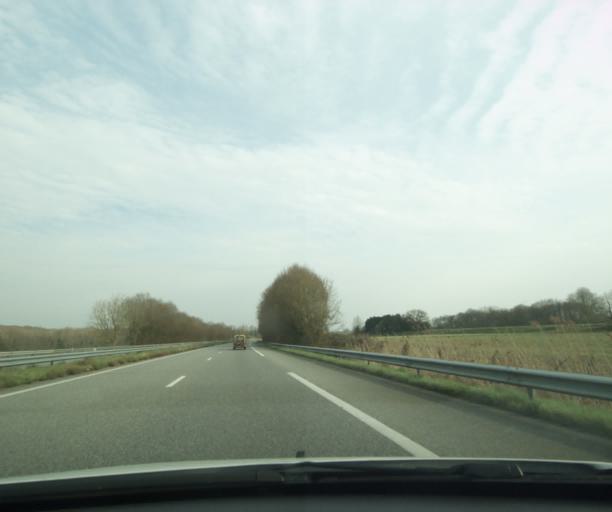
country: FR
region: Aquitaine
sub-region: Departement des Pyrenees-Atlantiques
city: Mont
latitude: 43.4570
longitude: -0.7043
